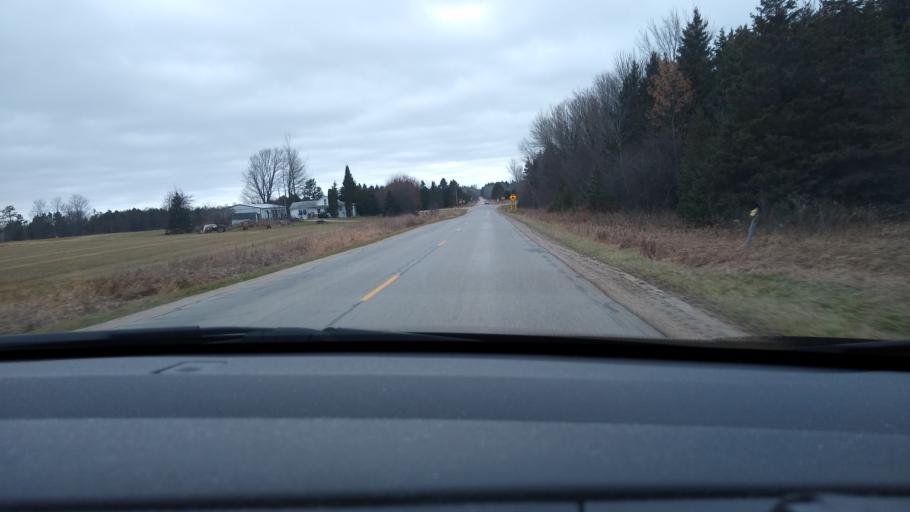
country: US
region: Michigan
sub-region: Missaukee County
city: Lake City
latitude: 44.3349
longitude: -85.0550
